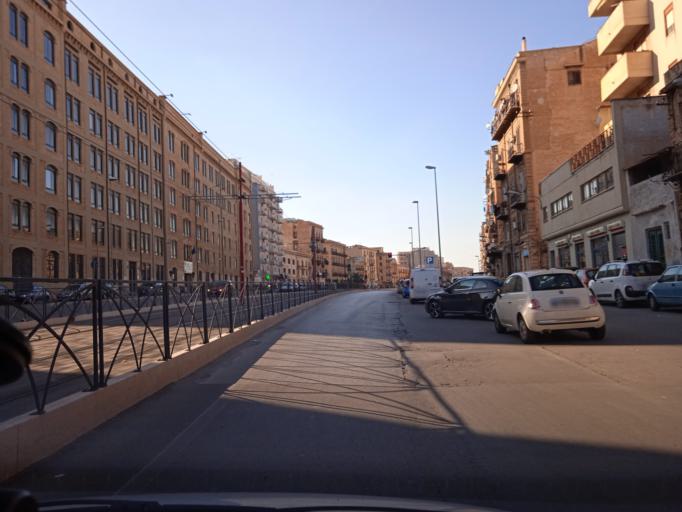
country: IT
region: Sicily
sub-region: Palermo
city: Palermo
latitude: 38.1074
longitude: 13.3724
